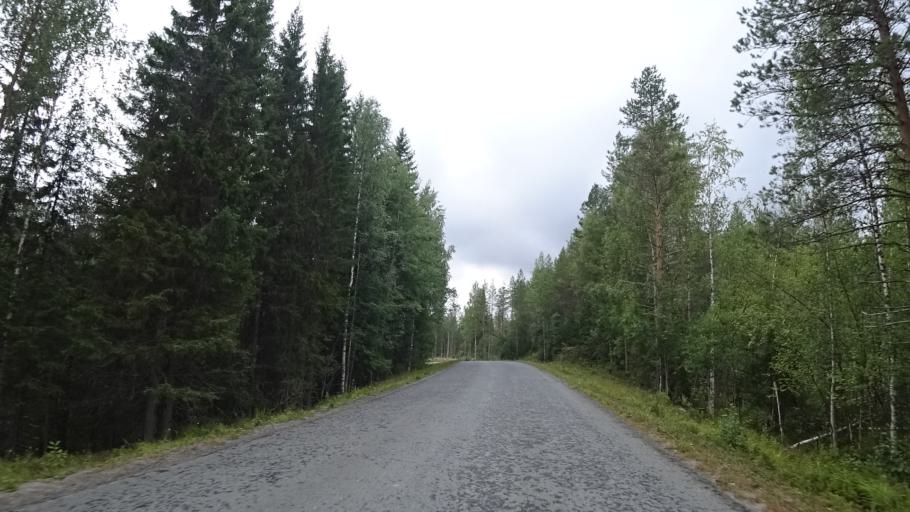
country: FI
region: North Karelia
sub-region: Joensuu
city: Ilomantsi
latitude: 62.9801
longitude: 31.2821
